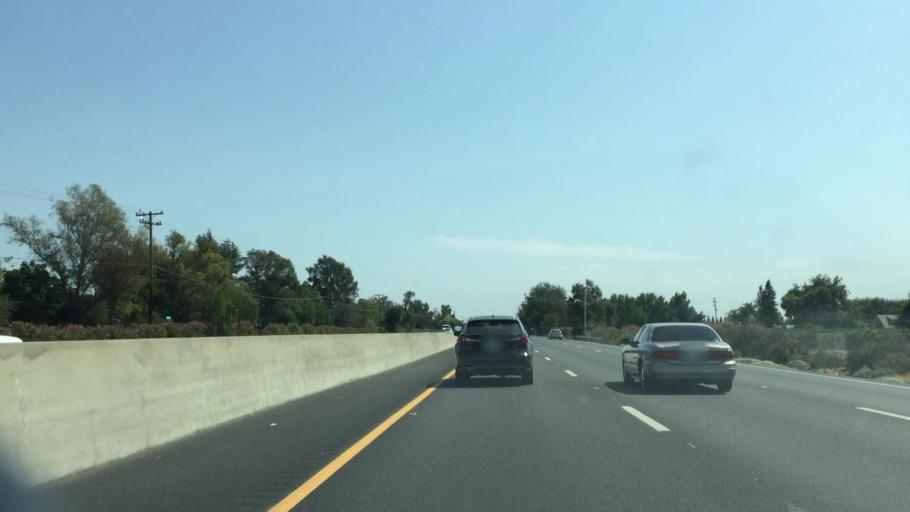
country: US
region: California
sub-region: San Joaquin County
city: Morada
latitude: 38.0709
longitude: -121.2598
